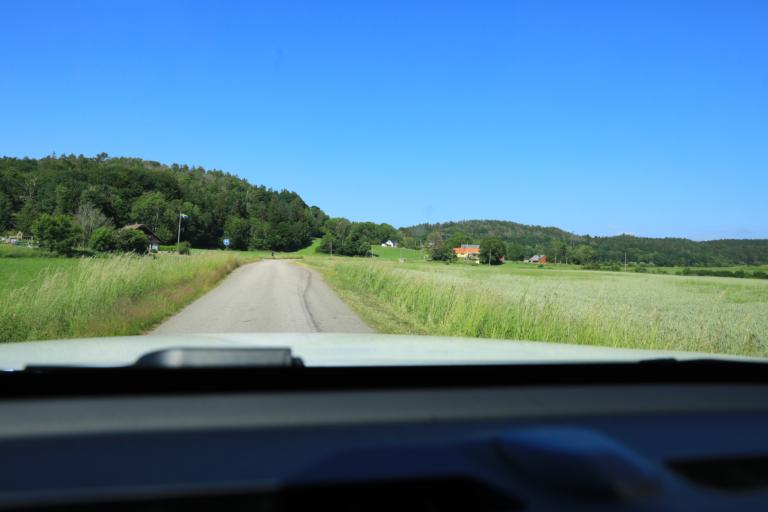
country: SE
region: Halland
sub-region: Varbergs Kommun
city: Veddige
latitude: 57.1848
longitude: 12.3135
